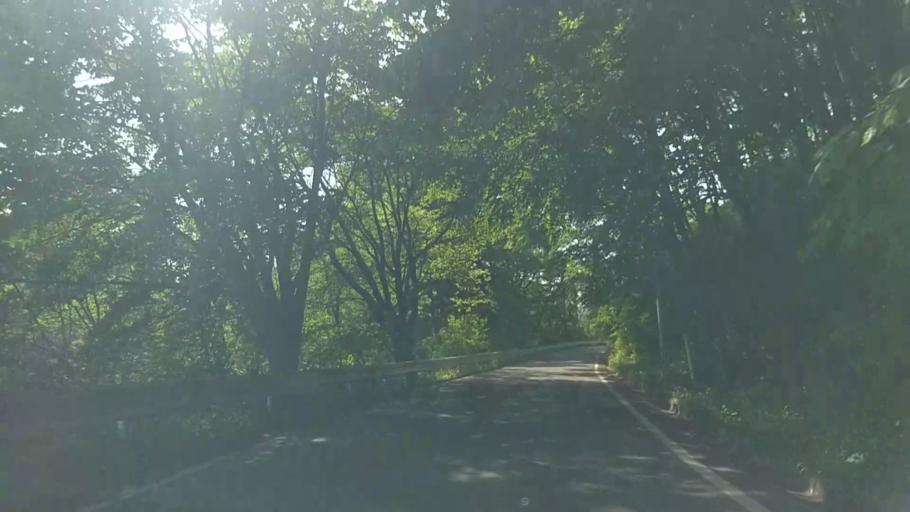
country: JP
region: Nagano
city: Saku
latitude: 36.1111
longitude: 138.4756
